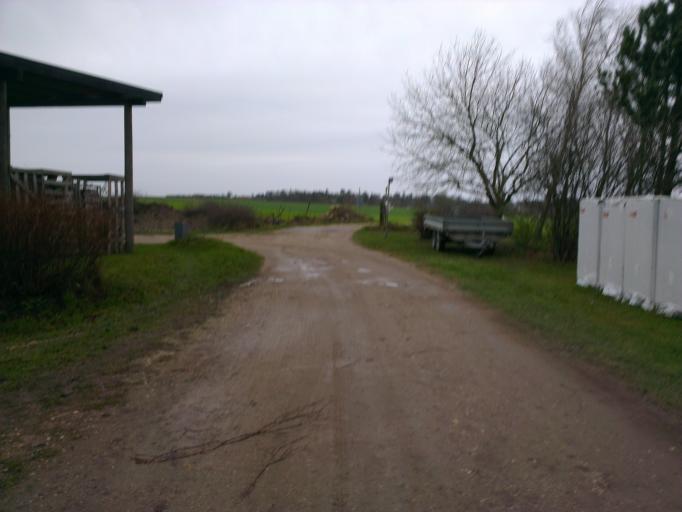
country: DK
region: Capital Region
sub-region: Frederikssund Kommune
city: Jaegerspris
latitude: 55.8422
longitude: 12.0116
